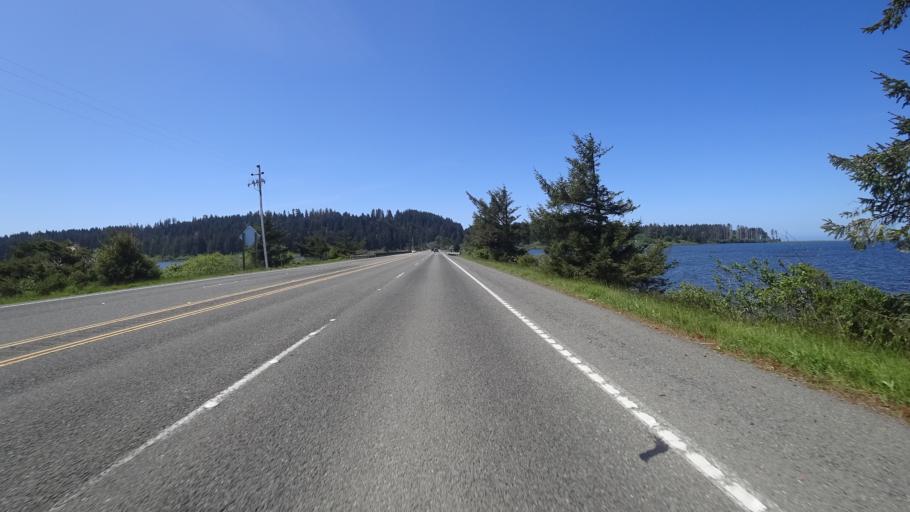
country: US
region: California
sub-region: Humboldt County
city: Westhaven-Moonstone
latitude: 41.1634
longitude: -124.1095
